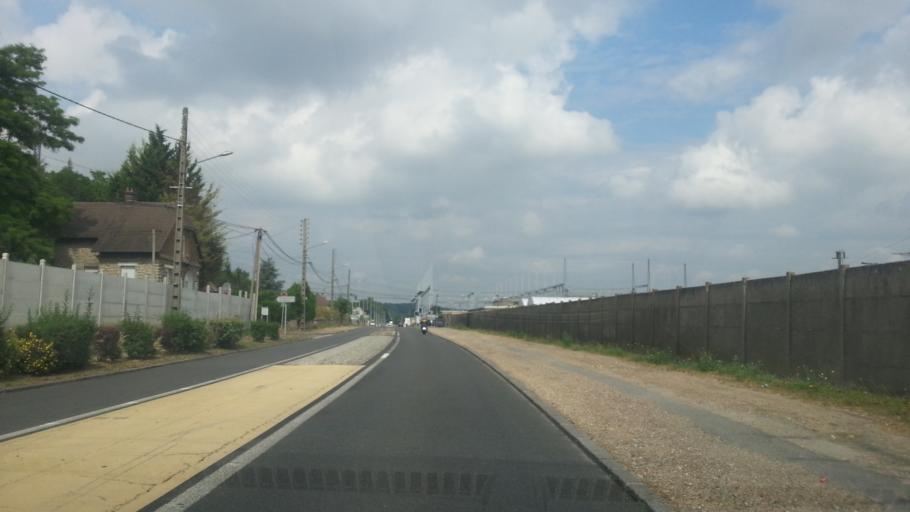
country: FR
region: Picardie
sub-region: Departement de l'Oise
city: Thiverny
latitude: 49.2393
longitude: 2.4389
